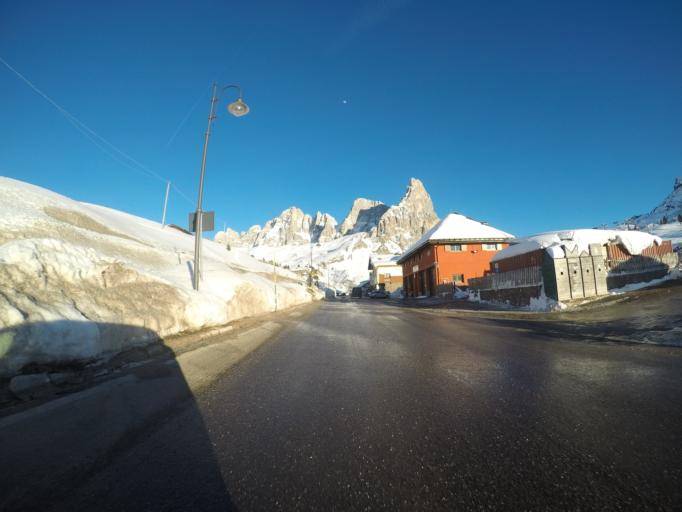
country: IT
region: Veneto
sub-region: Provincia di Belluno
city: Falcade Alto
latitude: 46.2964
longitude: 11.7854
